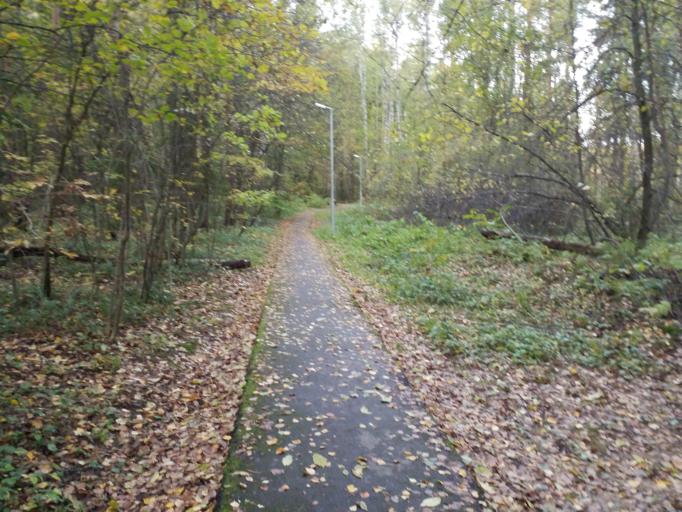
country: RU
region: Moskovskaya
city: Ashukino
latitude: 56.1609
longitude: 37.9578
